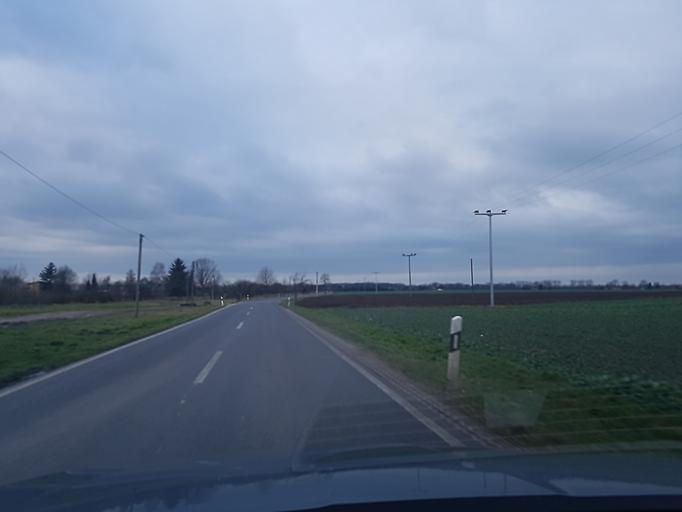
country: DE
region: Brandenburg
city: Sonnewalde
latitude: 51.6919
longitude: 13.6697
